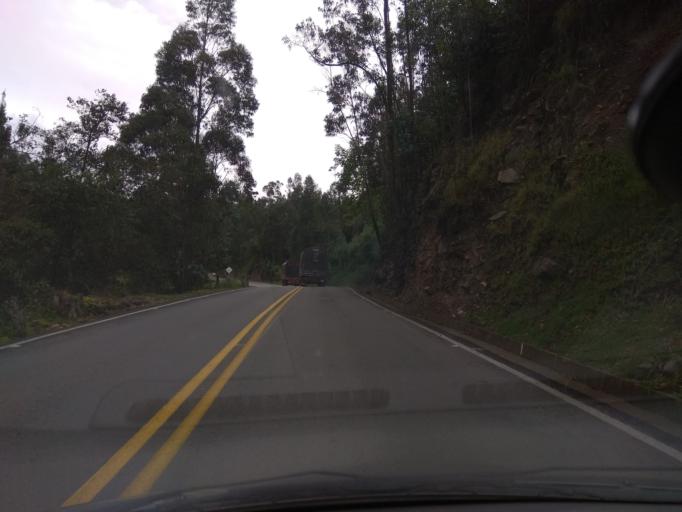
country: CO
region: Boyaca
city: Santa Rosa de Viterbo
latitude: 5.8586
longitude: -73.0124
